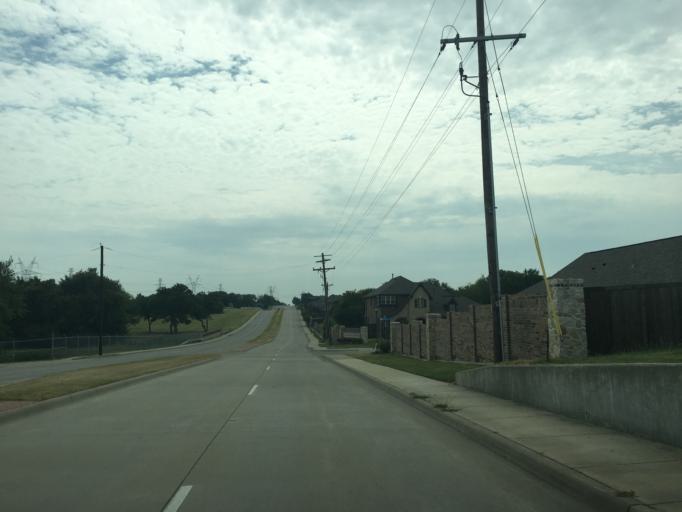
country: US
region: Texas
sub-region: Collin County
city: Wylie
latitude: 33.0169
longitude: -96.5261
